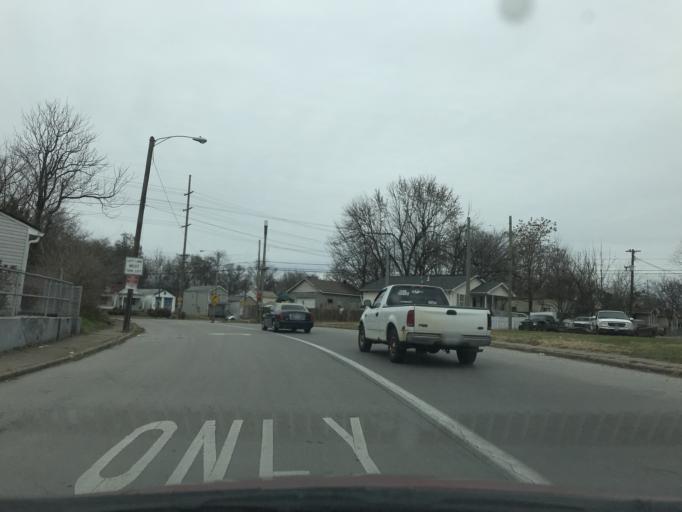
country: US
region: Kentucky
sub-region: Jefferson County
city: Louisville
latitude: 38.2627
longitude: -85.7848
